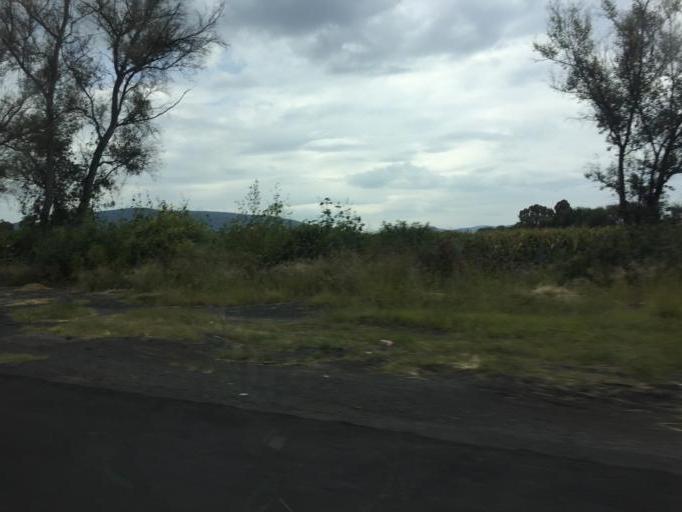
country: MX
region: Jalisco
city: Ocotlan
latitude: 20.3885
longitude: -102.7136
